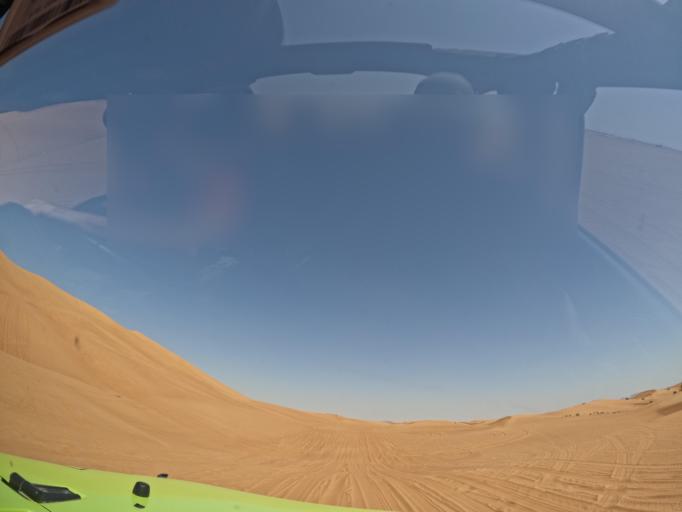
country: AE
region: Ash Shariqah
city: Adh Dhayd
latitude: 24.9604
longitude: 55.7202
